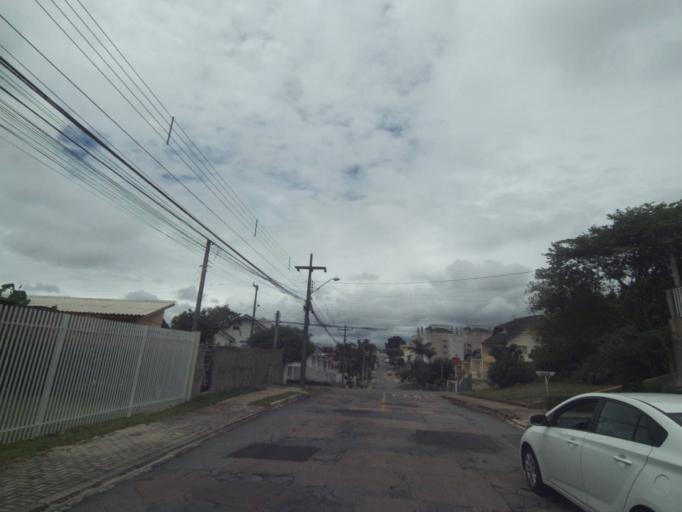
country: BR
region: Parana
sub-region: Curitiba
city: Curitiba
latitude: -25.4883
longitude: -49.2892
